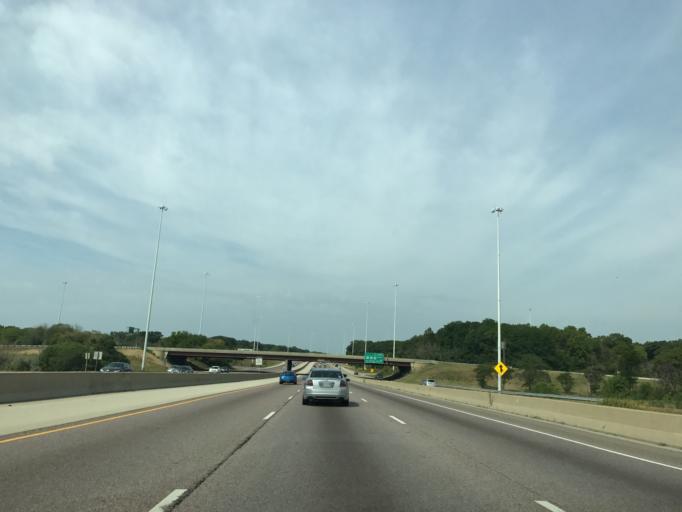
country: US
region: Illinois
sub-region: Cook County
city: Hodgkins
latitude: 41.7623
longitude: -87.8649
